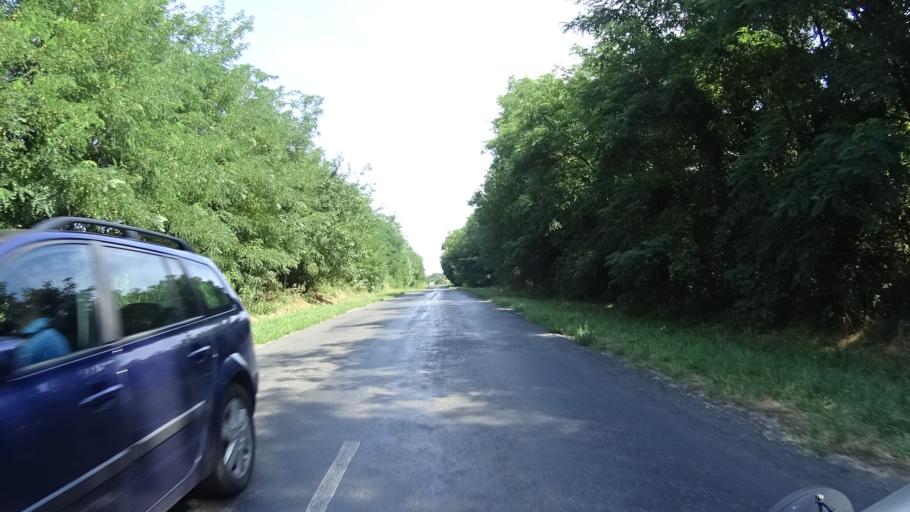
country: HU
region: Veszprem
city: Badacsonytomaj
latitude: 46.8236
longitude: 17.5144
